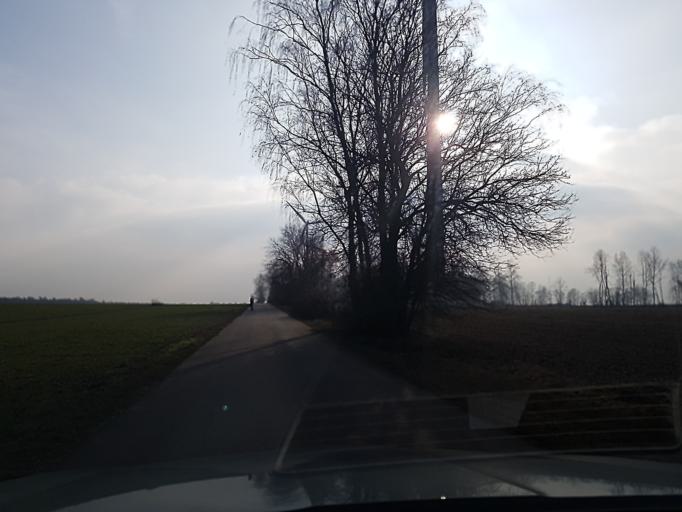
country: DE
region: Brandenburg
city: Doberlug-Kirchhain
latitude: 51.6204
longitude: 13.6049
